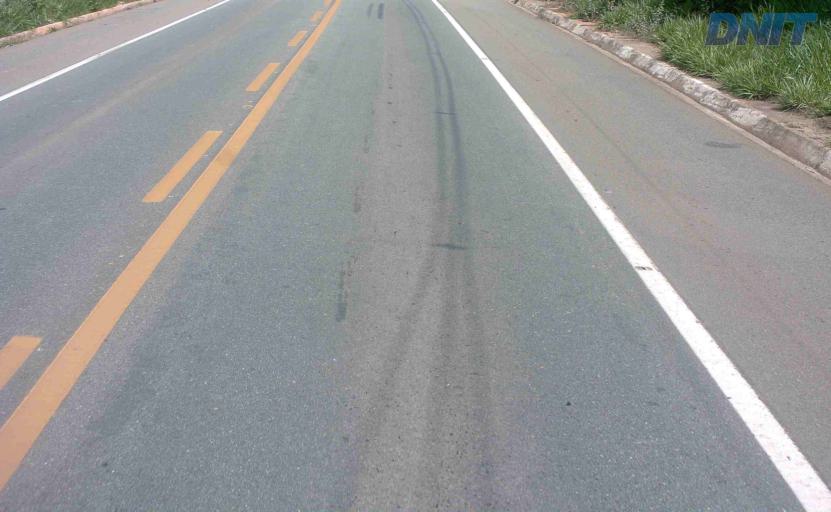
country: BR
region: Minas Gerais
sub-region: Governador Valadares
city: Governador Valadares
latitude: -18.8428
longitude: -41.9712
